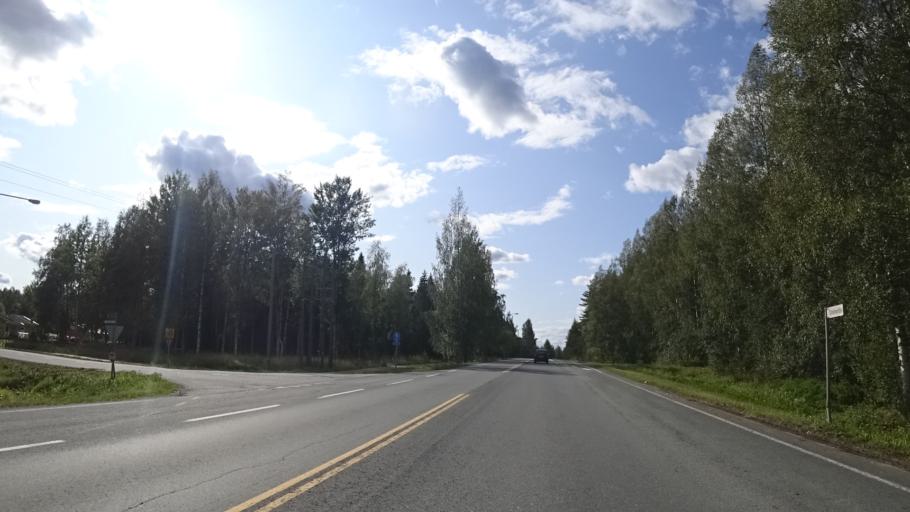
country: FI
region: North Karelia
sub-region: Keski-Karjala
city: Tohmajaervi
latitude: 62.2221
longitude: 30.3554
